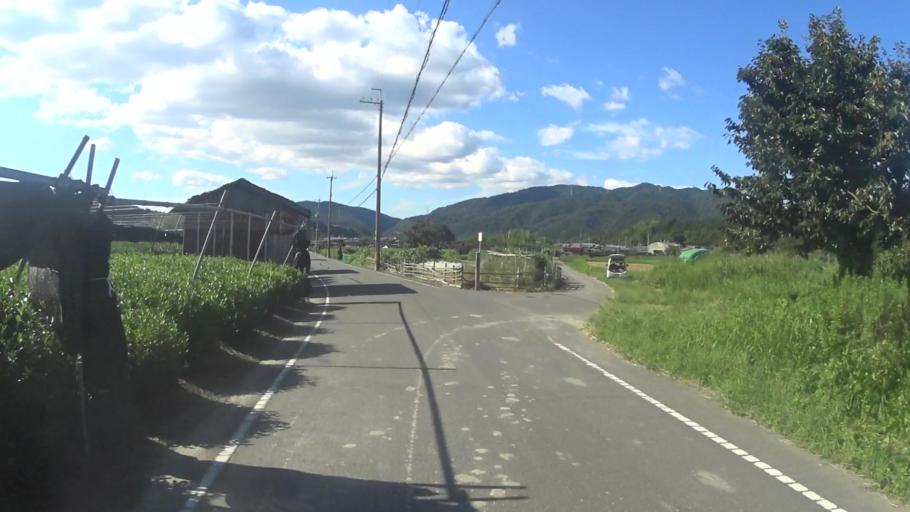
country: JP
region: Kyoto
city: Uji
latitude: 34.8370
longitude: 135.8601
